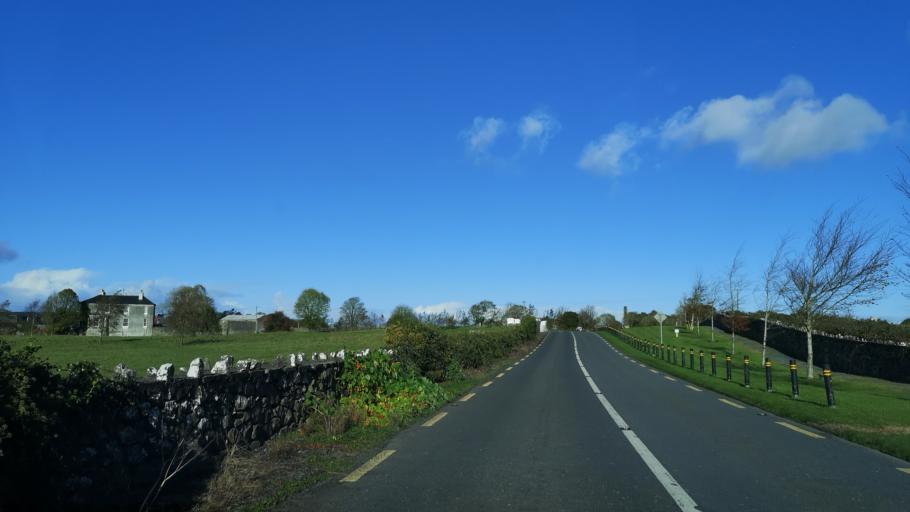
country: IE
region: Connaught
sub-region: Maigh Eo
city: Ballinrobe
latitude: 53.5754
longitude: -9.1218
